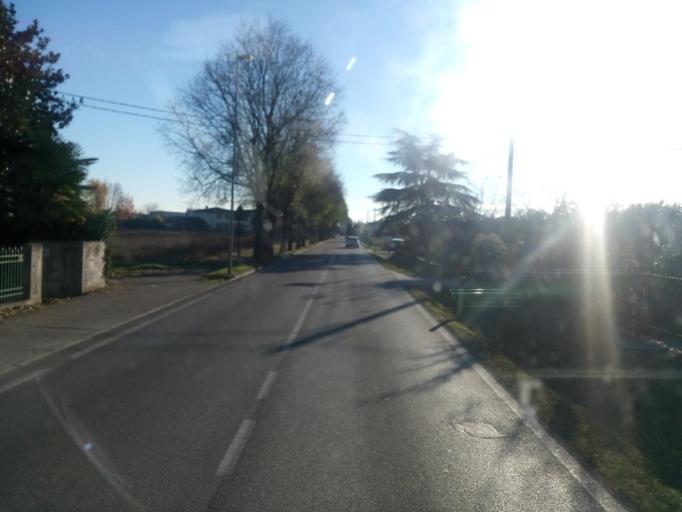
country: IT
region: Veneto
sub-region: Provincia di Vicenza
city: Rossano Veneto
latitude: 45.7029
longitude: 11.8168
